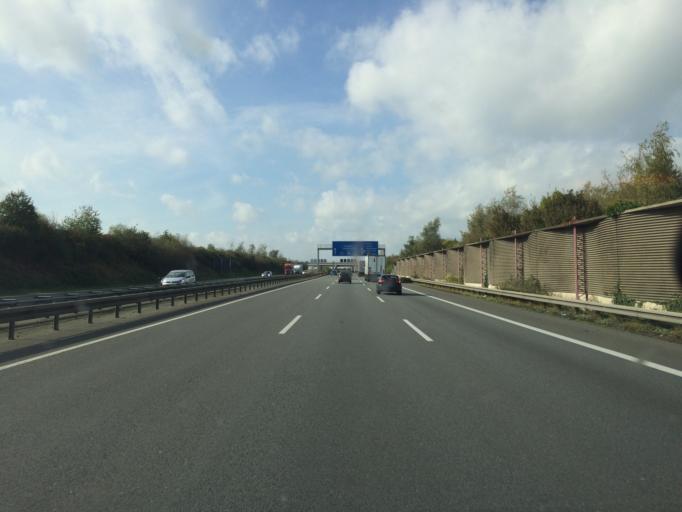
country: DE
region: Lower Saxony
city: Peine
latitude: 52.3358
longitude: 10.2793
